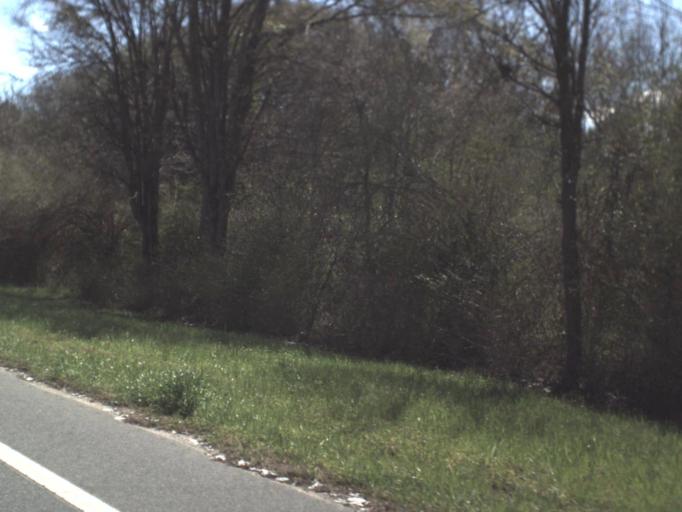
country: US
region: Florida
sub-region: Gadsden County
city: Gretna
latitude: 30.6401
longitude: -84.6760
